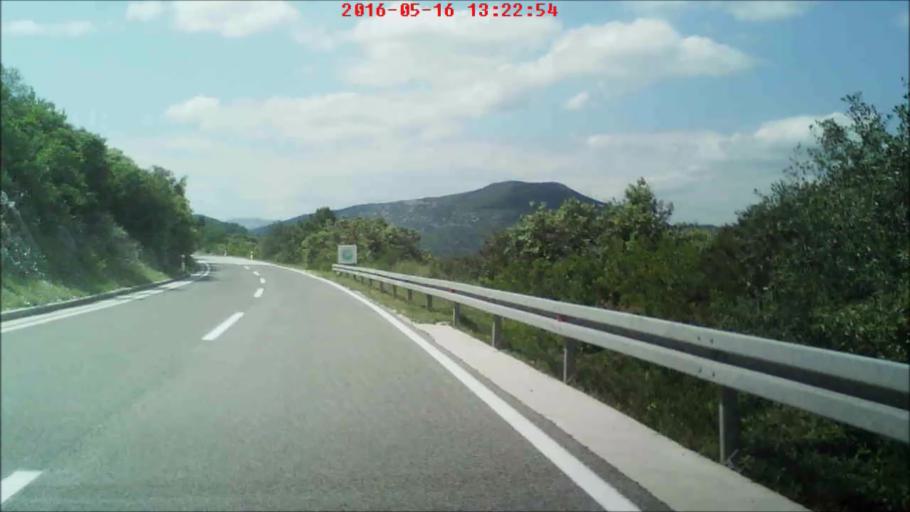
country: HR
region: Dubrovacko-Neretvanska
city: Ston
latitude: 42.8380
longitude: 17.7181
